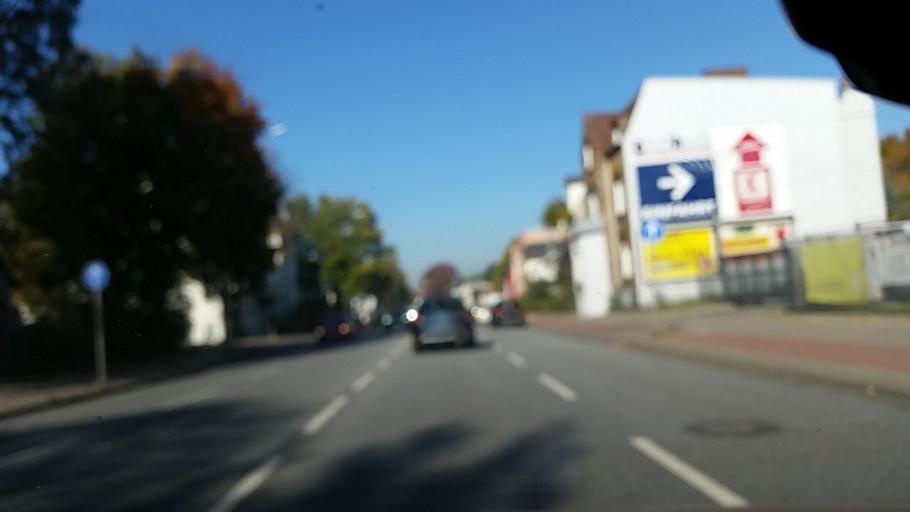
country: DE
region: Hamburg
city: Eidelstedt
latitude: 53.5828
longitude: 9.8818
